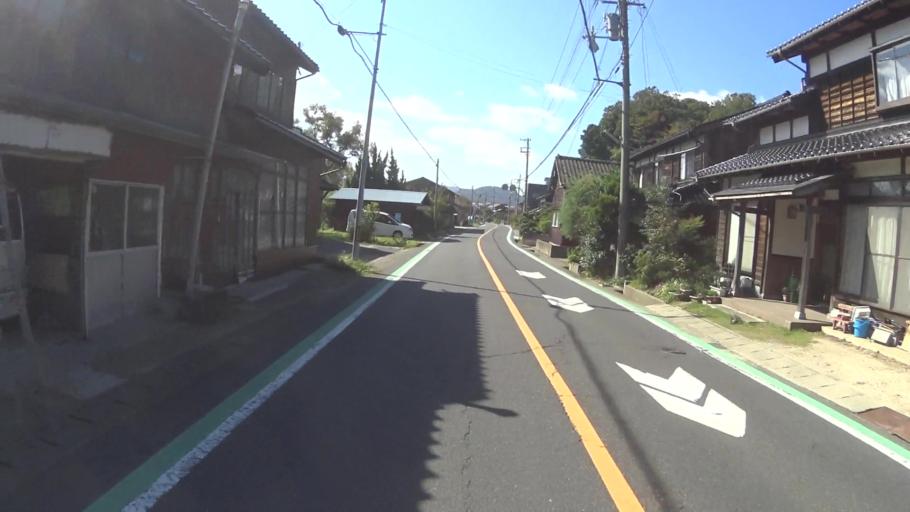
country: JP
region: Kyoto
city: Miyazu
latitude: 35.6935
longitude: 135.0369
